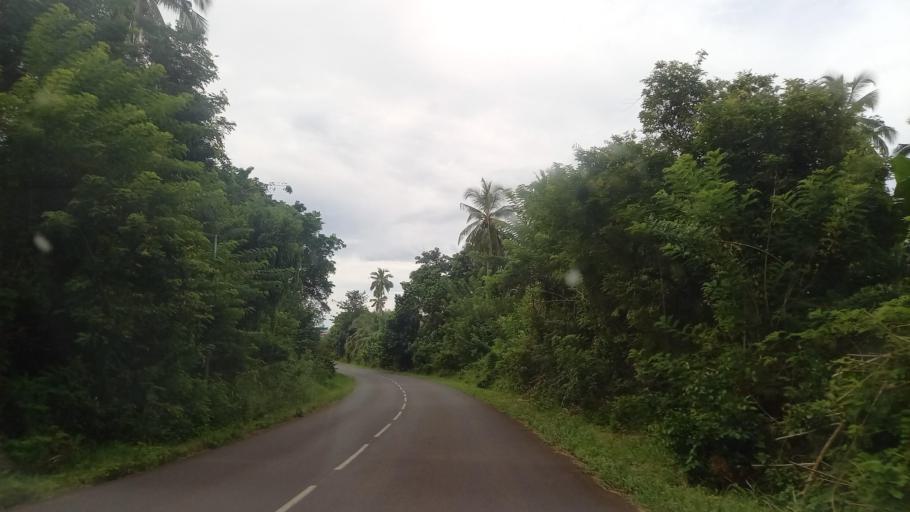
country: YT
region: Boueni
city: Boueni
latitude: -12.9095
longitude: 45.1011
